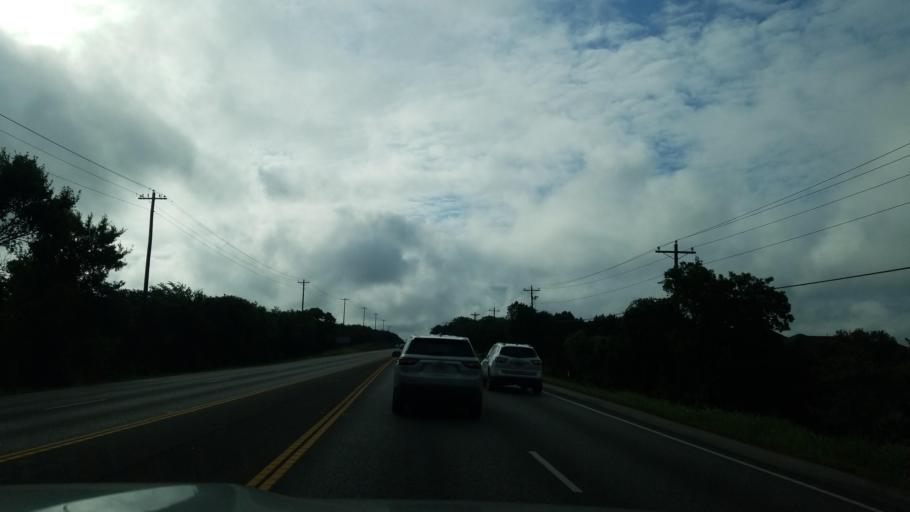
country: US
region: Texas
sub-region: Travis County
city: Barton Creek
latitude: 30.2348
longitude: -97.9069
